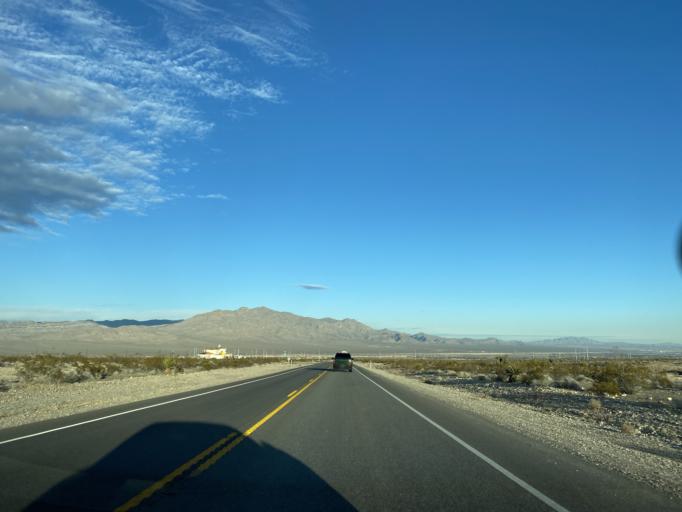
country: US
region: Nevada
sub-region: Clark County
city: Summerlin South
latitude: 36.3218
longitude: -115.3531
